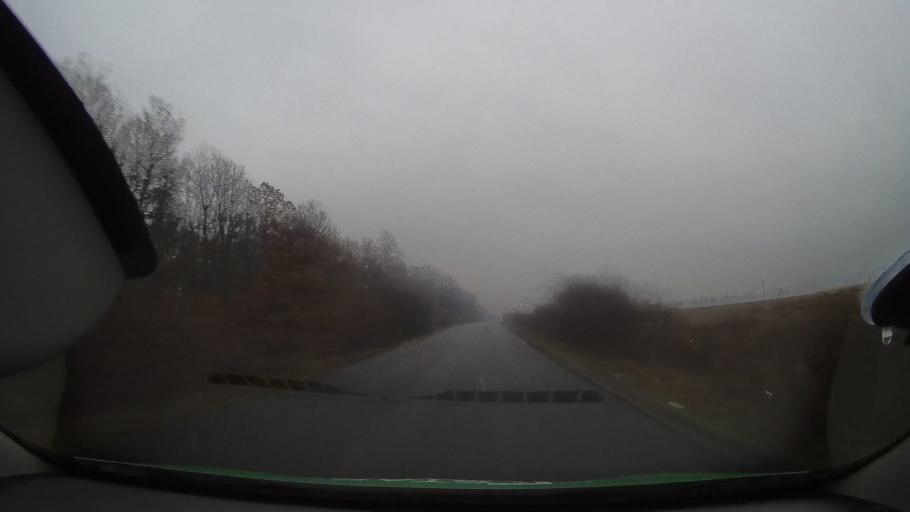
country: RO
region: Bihor
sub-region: Comuna Tinca
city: Gurbediu
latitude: 46.7787
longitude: 21.8758
